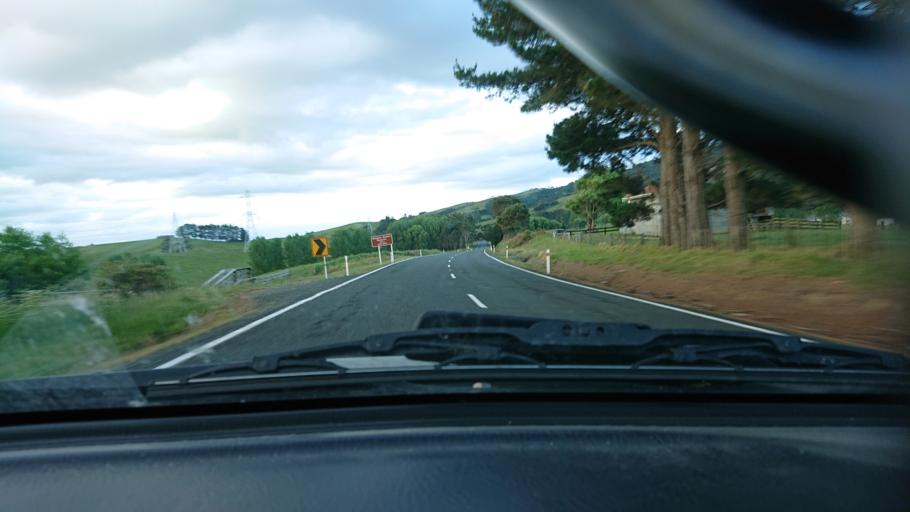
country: NZ
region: Auckland
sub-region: Auckland
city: Parakai
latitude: -36.4680
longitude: 174.4465
